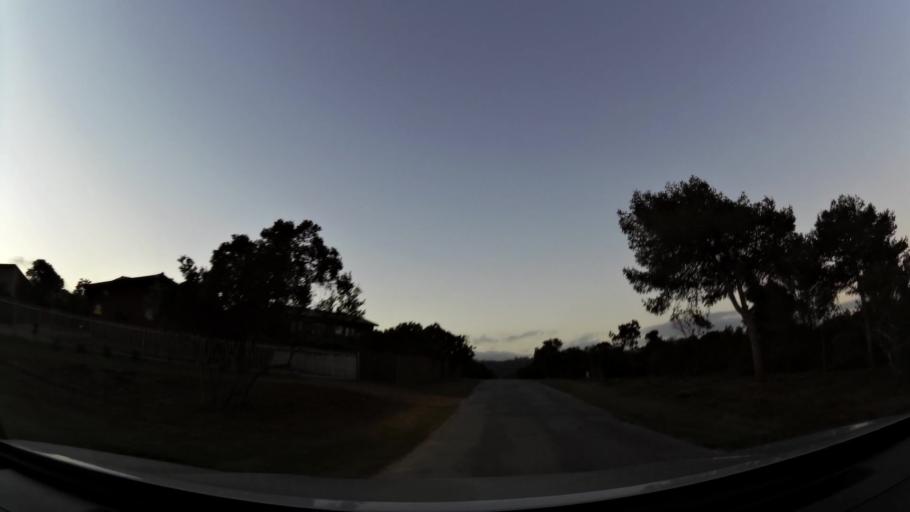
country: ZA
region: Western Cape
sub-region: Eden District Municipality
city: Knysna
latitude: -34.0280
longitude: 22.8064
